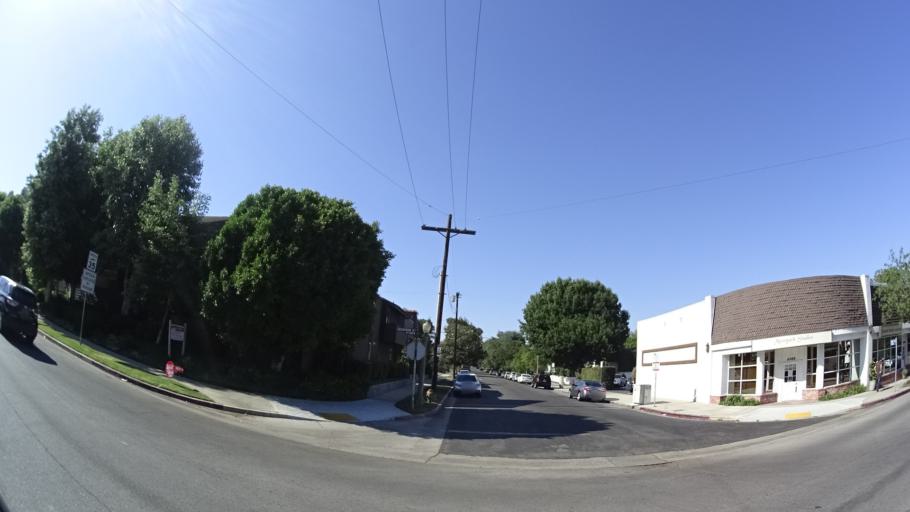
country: US
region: California
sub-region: Los Angeles County
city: North Hollywood
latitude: 34.1504
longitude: -118.3803
